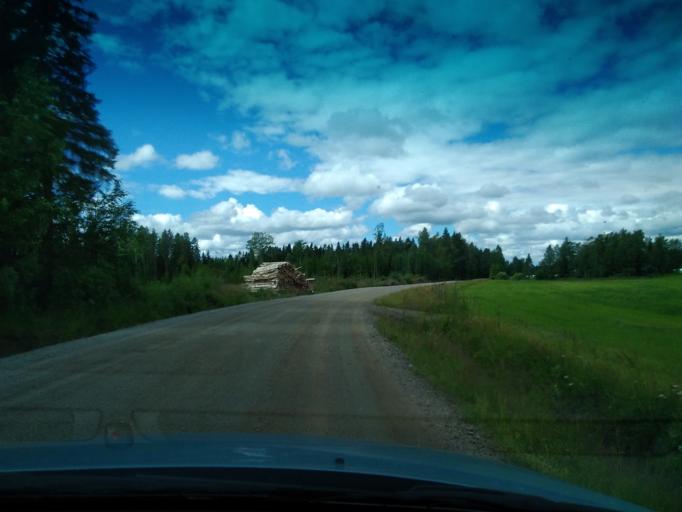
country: FI
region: Central Finland
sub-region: Saarijaervi-Viitasaari
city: Karstula
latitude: 62.7895
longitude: 24.9760
